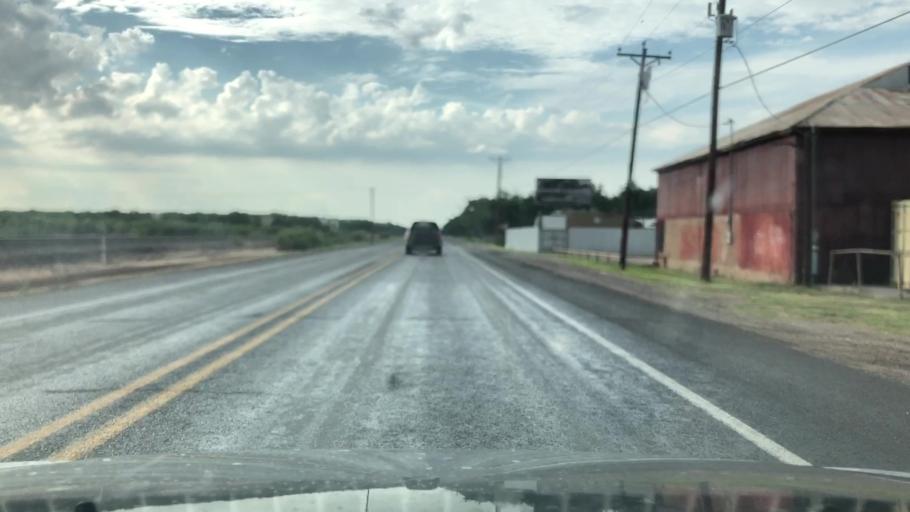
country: US
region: New Mexico
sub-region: Dona Ana County
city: Mesquite
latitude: 32.2094
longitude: -106.7248
